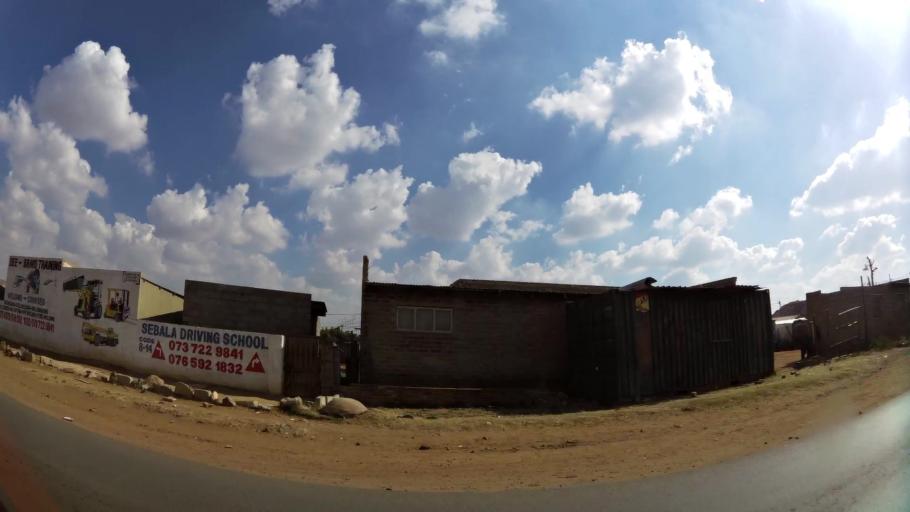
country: ZA
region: Gauteng
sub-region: City of Johannesburg Metropolitan Municipality
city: Roodepoort
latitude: -26.1881
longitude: 27.8679
